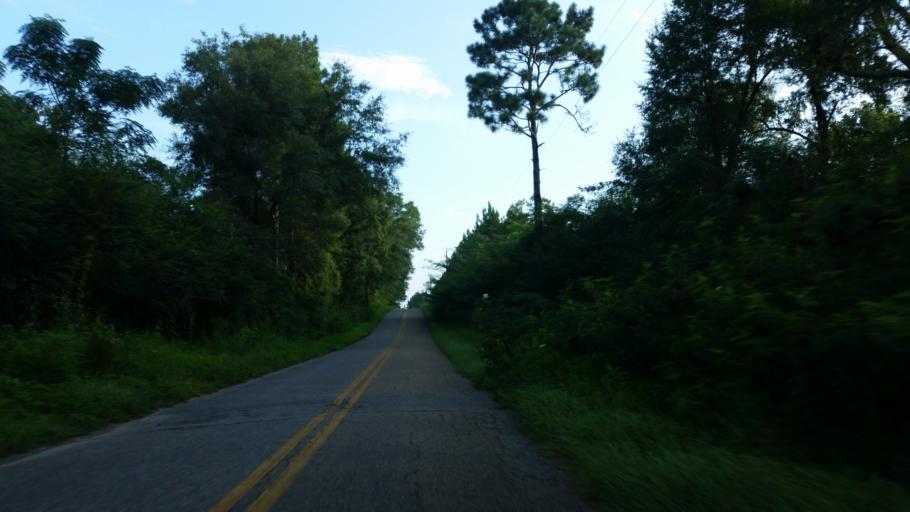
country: US
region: Alabama
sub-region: Escambia County
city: Atmore
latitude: 30.9787
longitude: -87.5712
